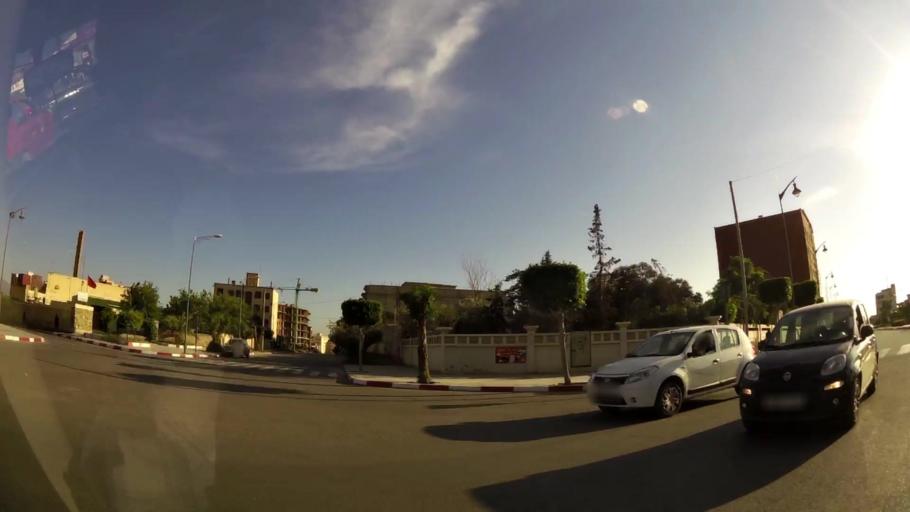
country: MA
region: Oriental
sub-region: Oujda-Angad
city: Oujda
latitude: 34.6913
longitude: -1.9111
